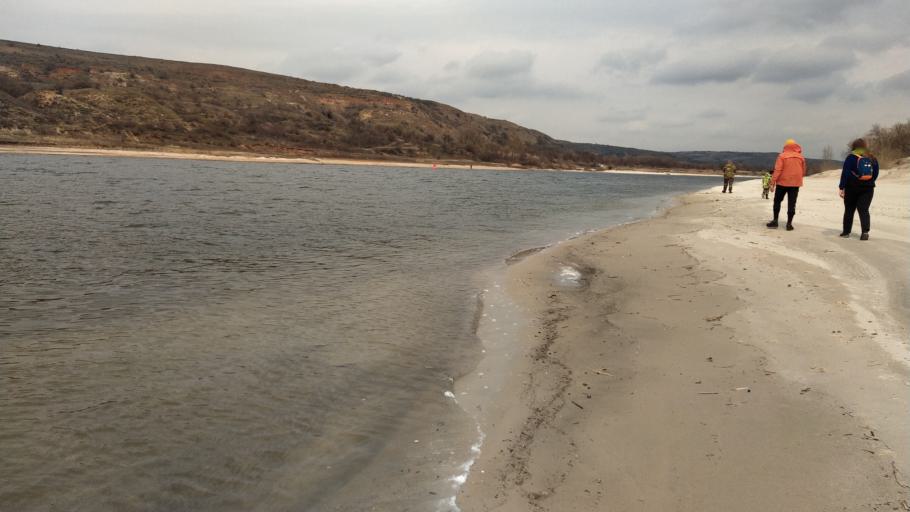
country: RU
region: Rostov
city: Semikarakorsk
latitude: 47.5576
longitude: 40.6729
